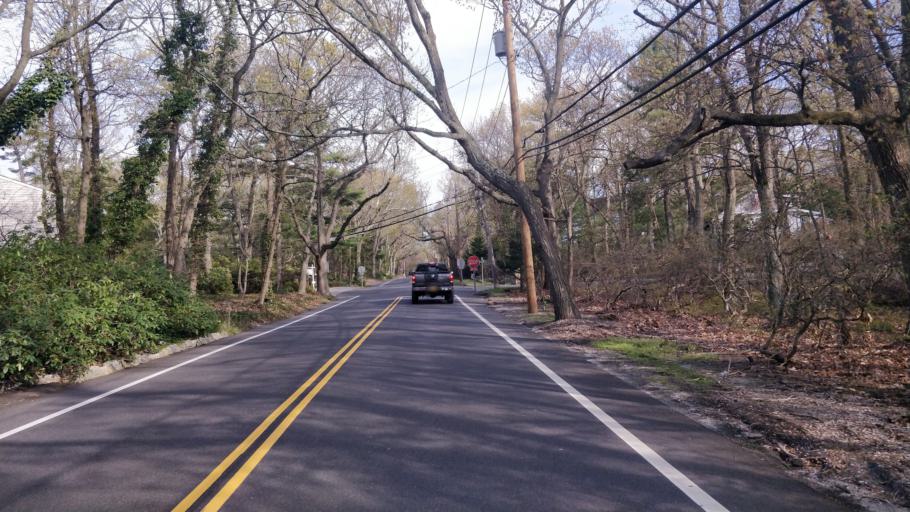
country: US
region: New York
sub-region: Suffolk County
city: Stony Brook
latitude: 40.9421
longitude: -73.1340
